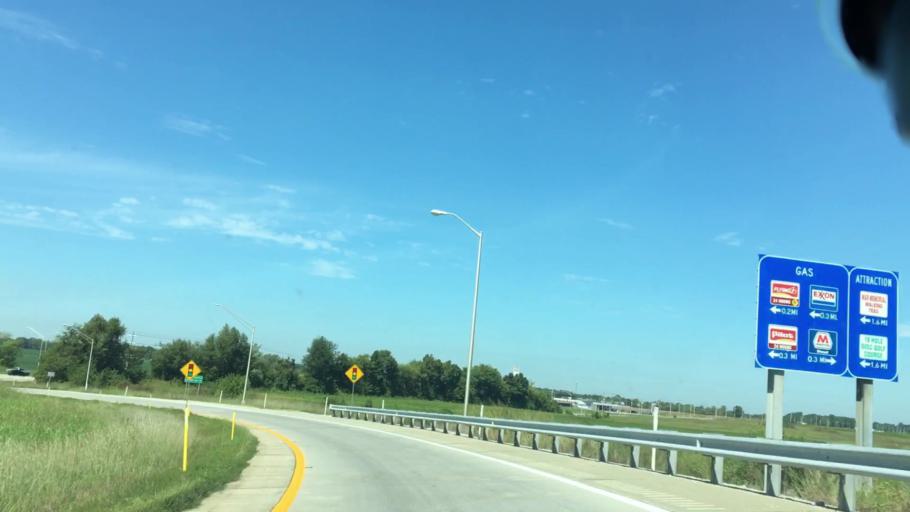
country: US
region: Kentucky
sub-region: Christian County
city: Oak Grove
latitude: 36.7042
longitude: -87.4530
